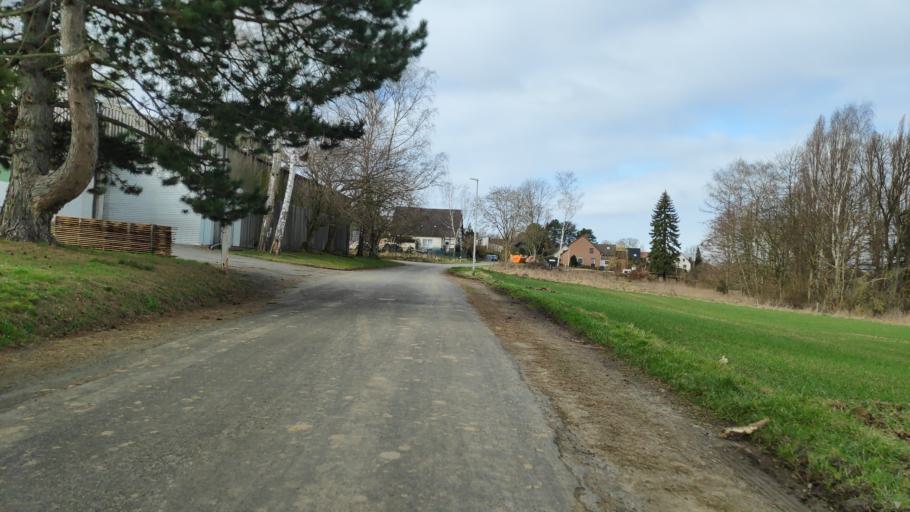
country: DE
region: North Rhine-Westphalia
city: Porta Westfalica
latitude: 52.2563
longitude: 8.8799
